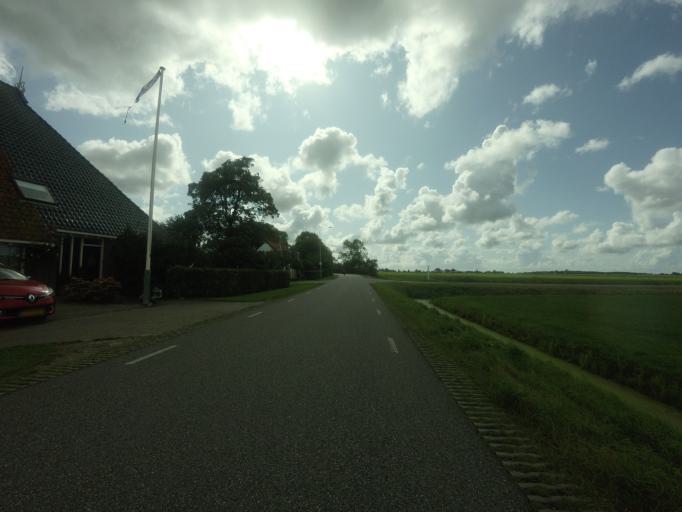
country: NL
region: Friesland
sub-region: Sudwest Fryslan
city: IJlst
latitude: 53.0507
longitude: 5.6062
